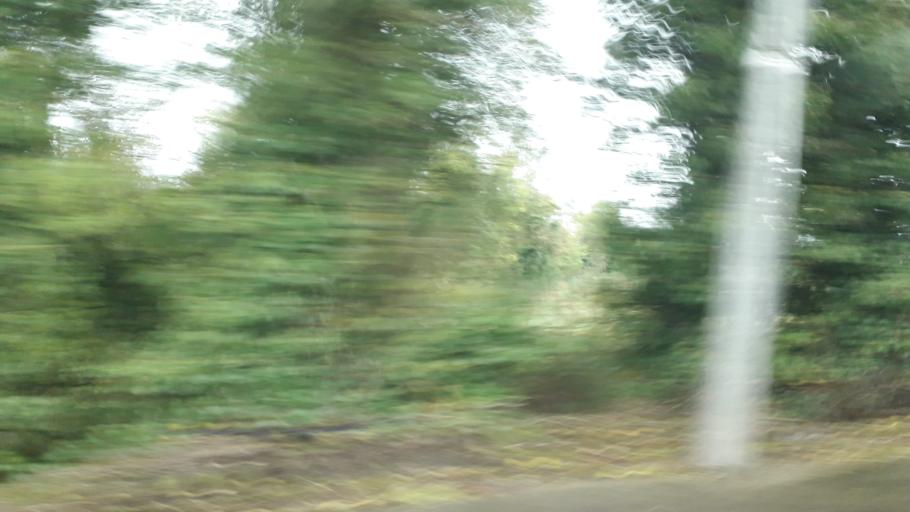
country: IE
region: Leinster
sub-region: An Longfort
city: Lanesborough
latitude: 53.7689
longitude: -8.1029
